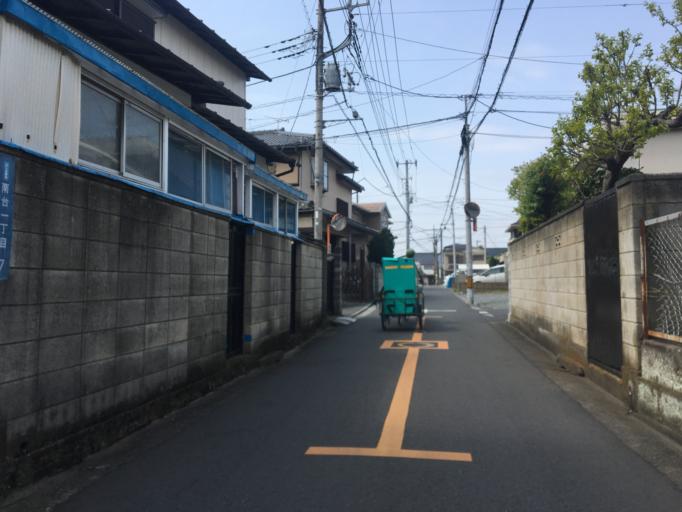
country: JP
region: Saitama
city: Kamifukuoka
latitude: 35.8705
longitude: 139.5192
